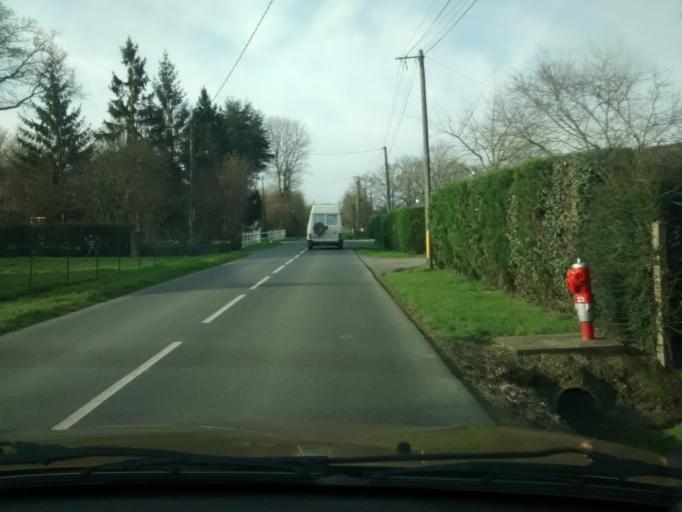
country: FR
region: Pays de la Loire
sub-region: Departement de la Loire-Atlantique
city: Notre-Dame-des-Landes
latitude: 47.3864
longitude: -1.7027
